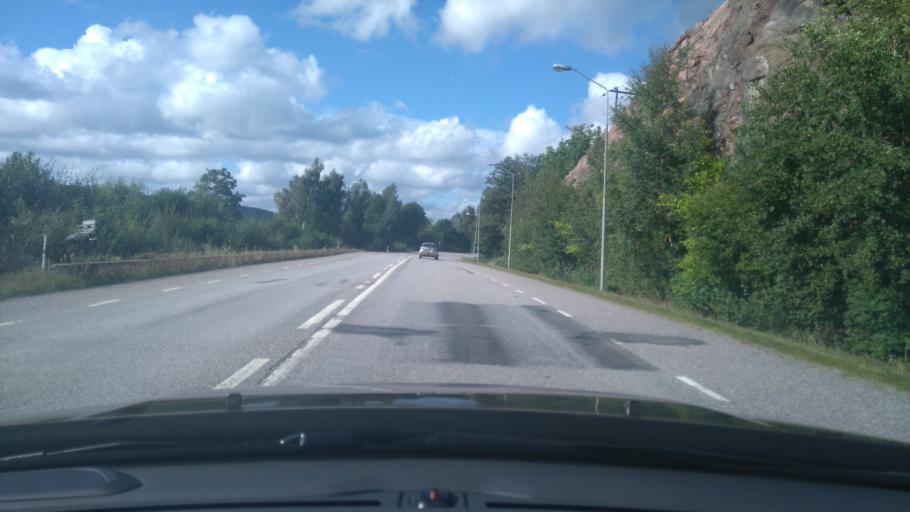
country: SE
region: Vaestra Goetaland
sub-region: Lilla Edets Kommun
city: Lodose
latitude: 58.0379
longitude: 12.1521
